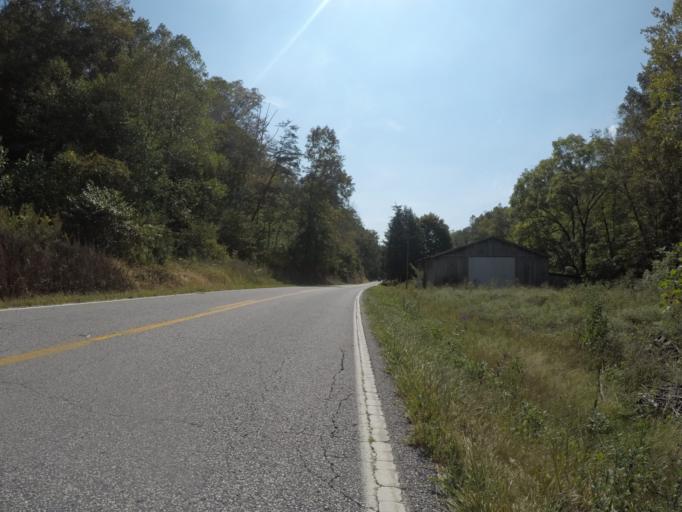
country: US
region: West Virginia
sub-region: Cabell County
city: Lesage
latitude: 38.5756
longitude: -82.4066
